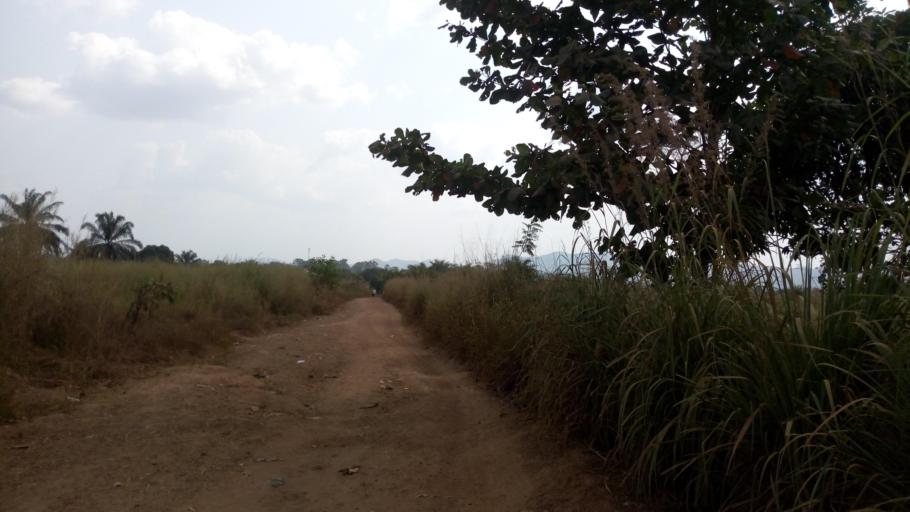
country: SL
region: Southern Province
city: Mogbwemo
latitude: 7.7782
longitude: -12.2986
